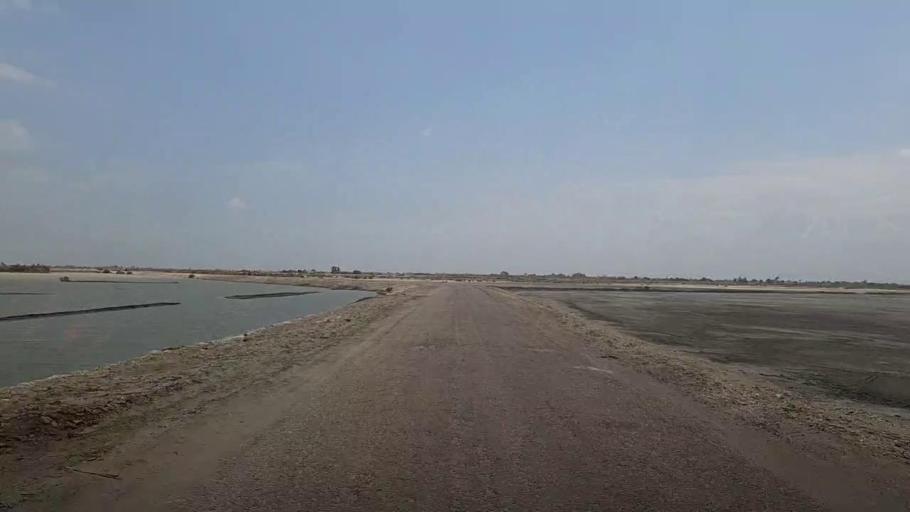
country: PK
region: Sindh
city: Kandhkot
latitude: 28.2864
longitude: 69.1561
